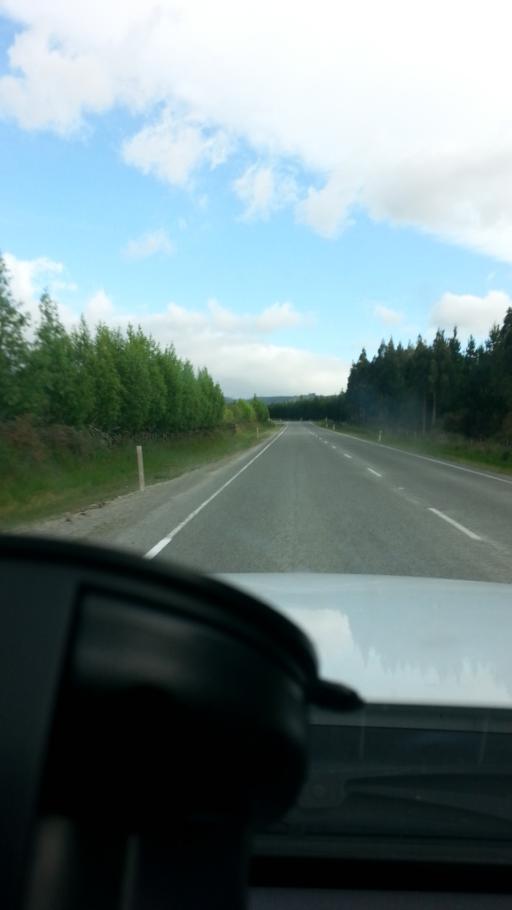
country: NZ
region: Wellington
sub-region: Masterton District
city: Masterton
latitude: -40.8059
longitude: 175.6198
